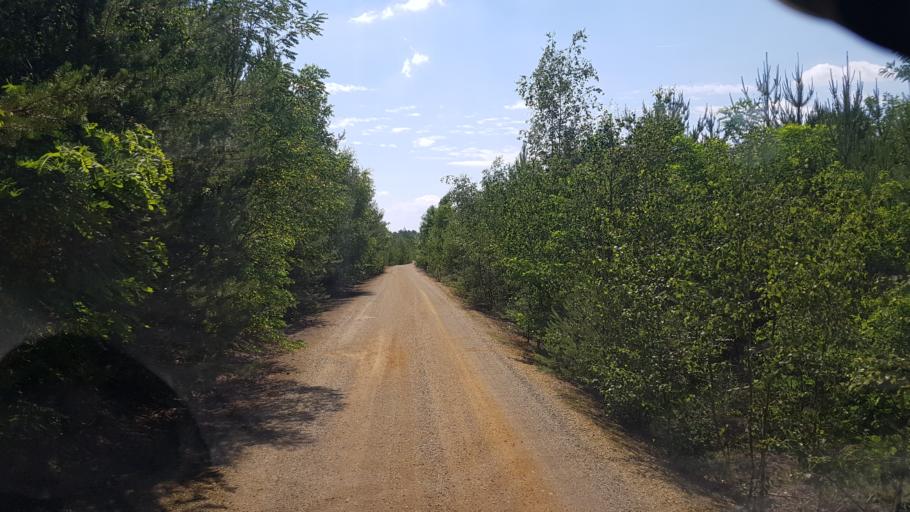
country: DE
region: Brandenburg
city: Sallgast
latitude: 51.5915
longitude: 13.7940
